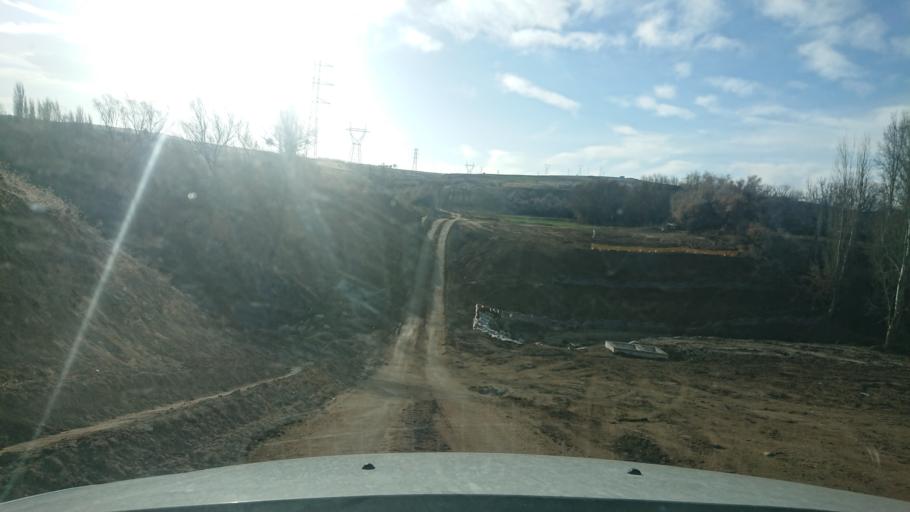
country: TR
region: Aksaray
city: Agacoren
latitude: 38.8614
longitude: 33.9415
